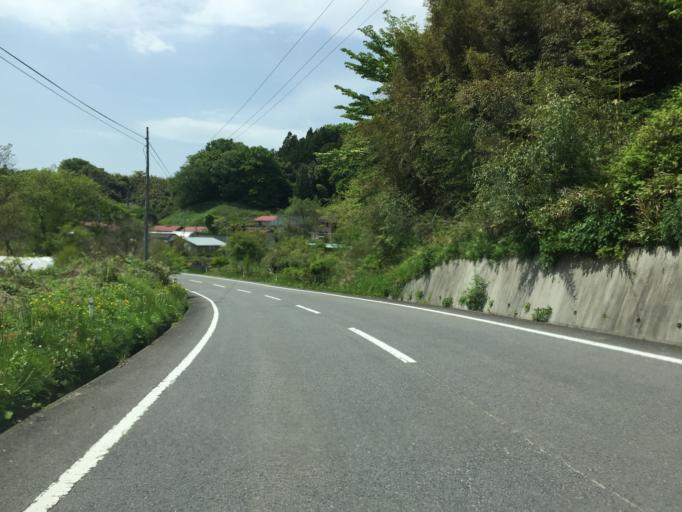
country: JP
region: Fukushima
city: Ishikawa
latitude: 37.1851
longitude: 140.5256
